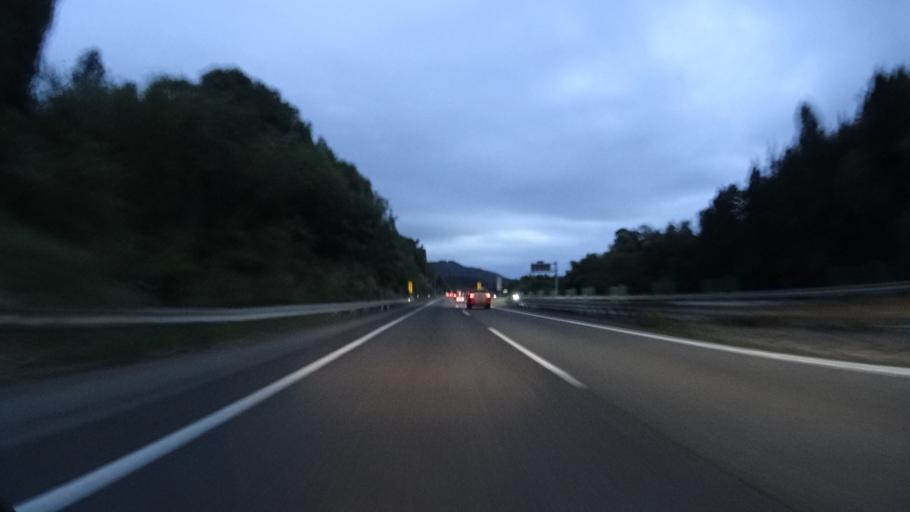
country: JP
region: Shiga Prefecture
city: Hikone
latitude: 35.2115
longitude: 136.2867
